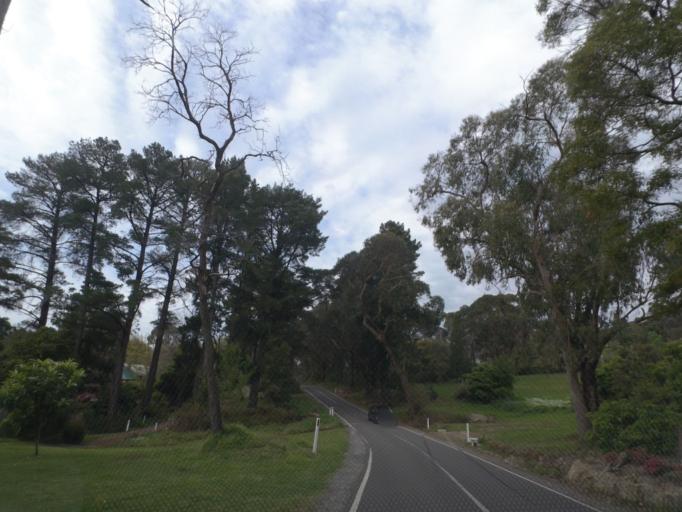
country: AU
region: Victoria
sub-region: Yarra Ranges
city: Montrose
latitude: -37.8164
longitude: 145.3495
